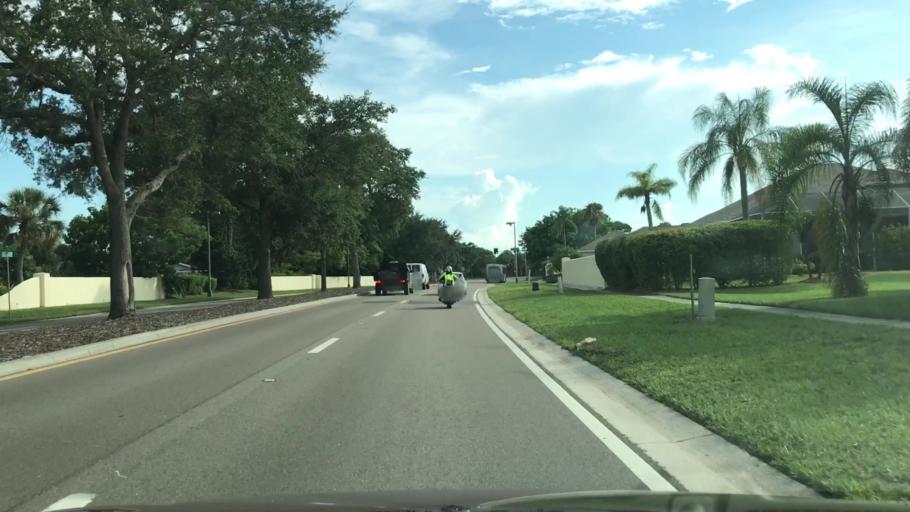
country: US
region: Florida
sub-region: Sarasota County
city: Venice Gardens
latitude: 27.0666
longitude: -82.3909
